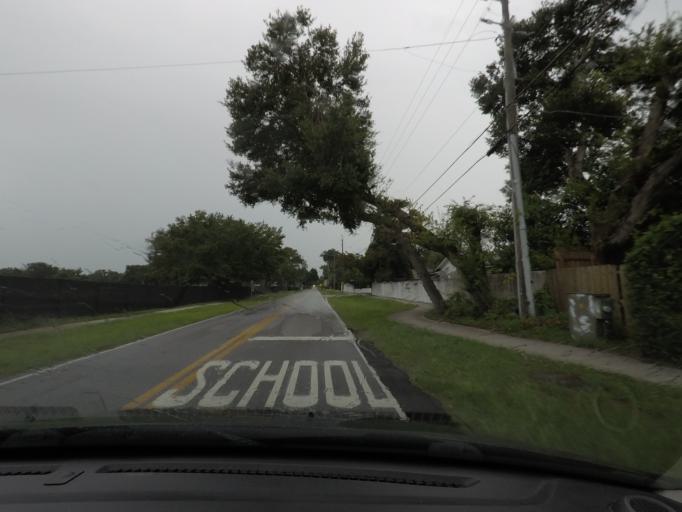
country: US
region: Florida
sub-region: Orange County
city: Edgewood
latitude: 28.4985
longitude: -81.3533
